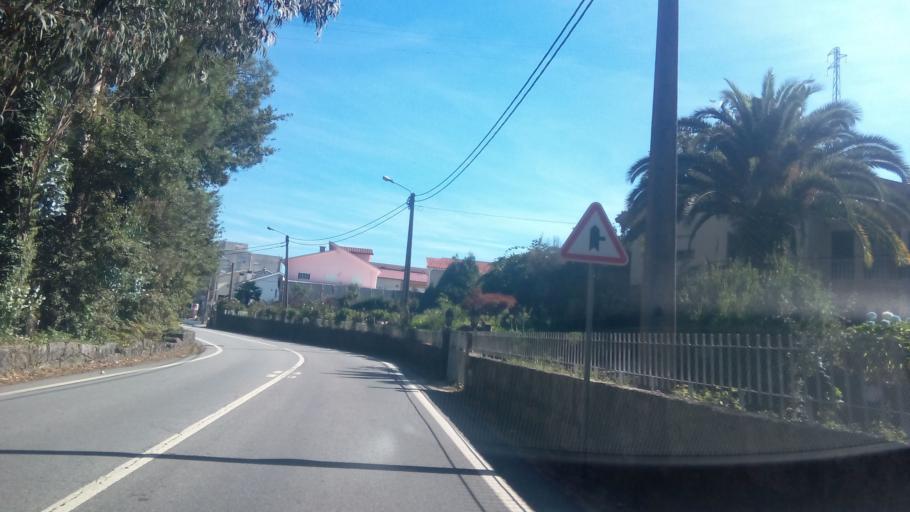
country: PT
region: Porto
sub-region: Paredes
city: Baltar
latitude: 41.1800
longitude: -8.3891
